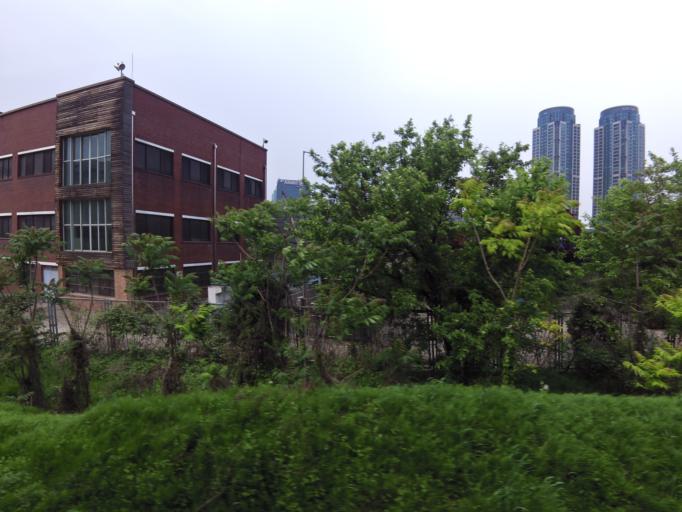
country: KR
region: Seoul
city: Seoul
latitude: 37.5142
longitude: 126.9312
